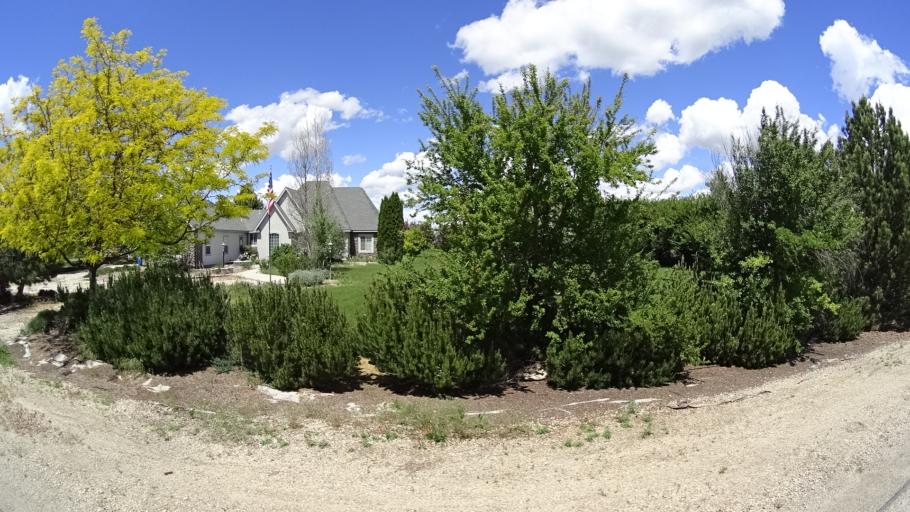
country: US
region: Idaho
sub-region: Ada County
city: Meridian
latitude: 43.5830
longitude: -116.4491
